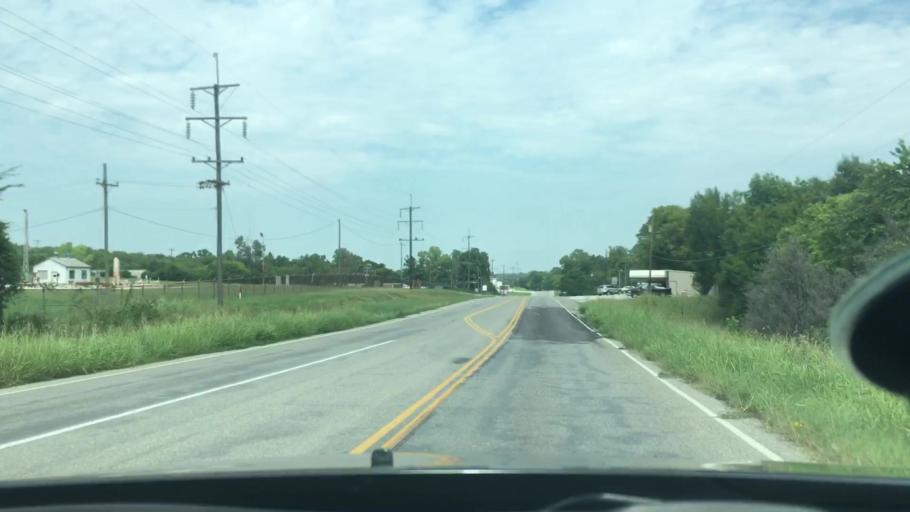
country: US
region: Oklahoma
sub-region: Pontotoc County
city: Byng
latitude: 34.8255
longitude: -96.6786
